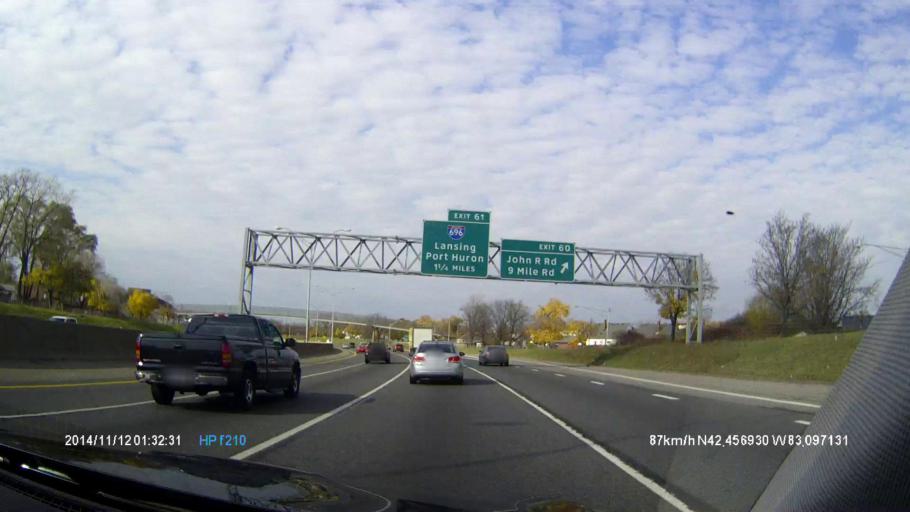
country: US
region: Michigan
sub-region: Oakland County
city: Hazel Park
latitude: 42.4572
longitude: -83.0975
